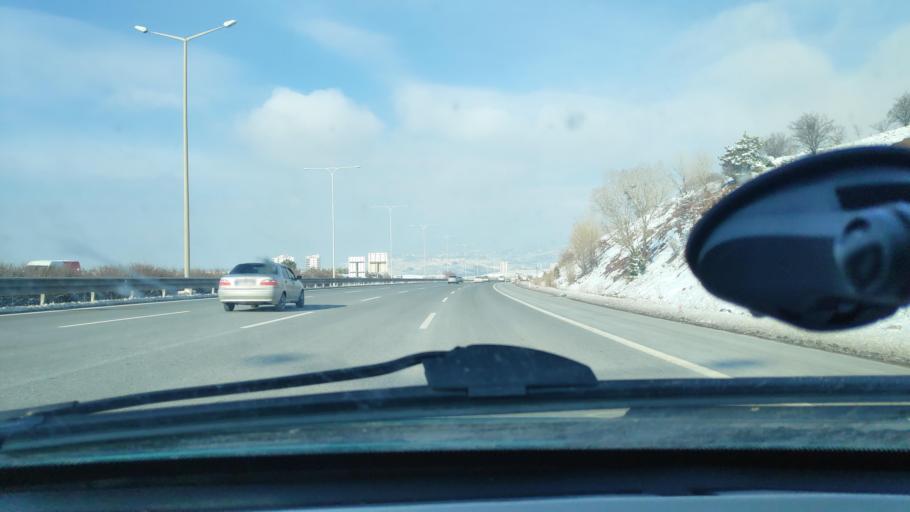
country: TR
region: Ankara
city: Batikent
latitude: 40.0192
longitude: 32.8161
